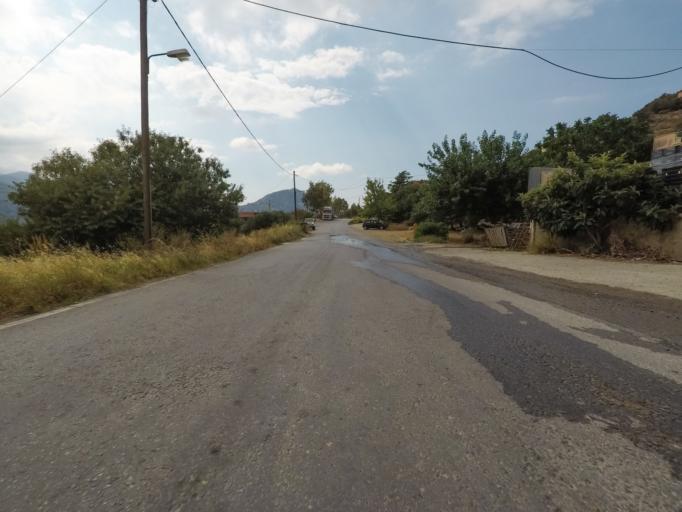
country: GR
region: Crete
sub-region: Nomos Lasithiou
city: Neapoli
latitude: 35.2603
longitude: 25.6117
